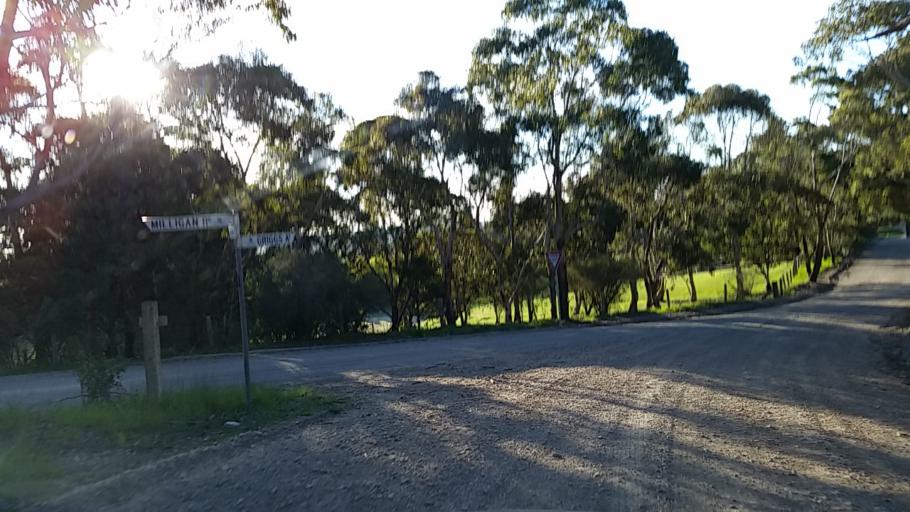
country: AU
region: South Australia
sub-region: Mount Barker
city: Meadows
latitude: -35.2284
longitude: 138.7370
